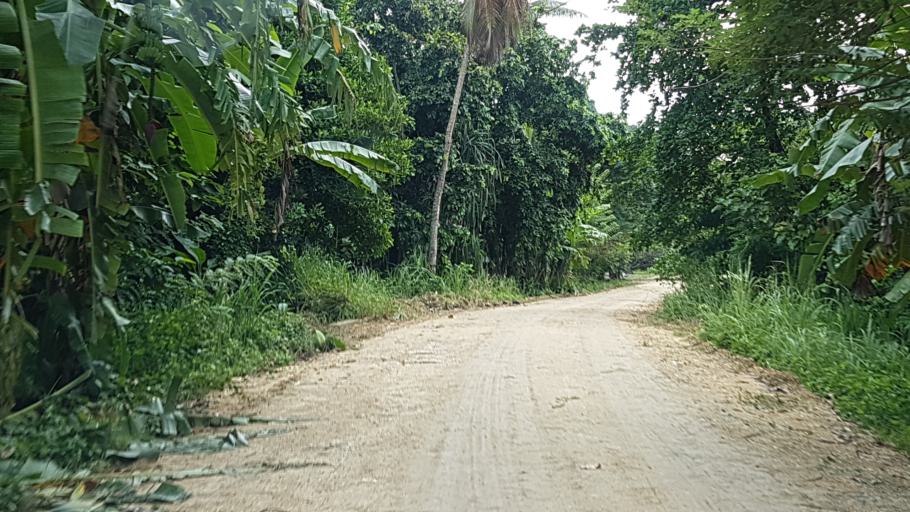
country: PG
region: Milne Bay
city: Alotau
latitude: -10.2903
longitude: 150.7667
